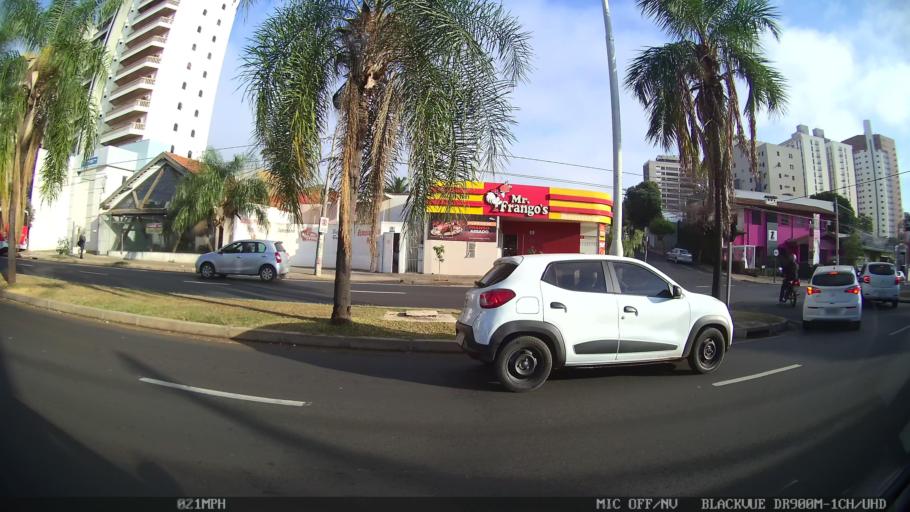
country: BR
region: Sao Paulo
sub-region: Sao Jose Do Rio Preto
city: Sao Jose do Rio Preto
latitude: -20.8187
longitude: -49.3825
